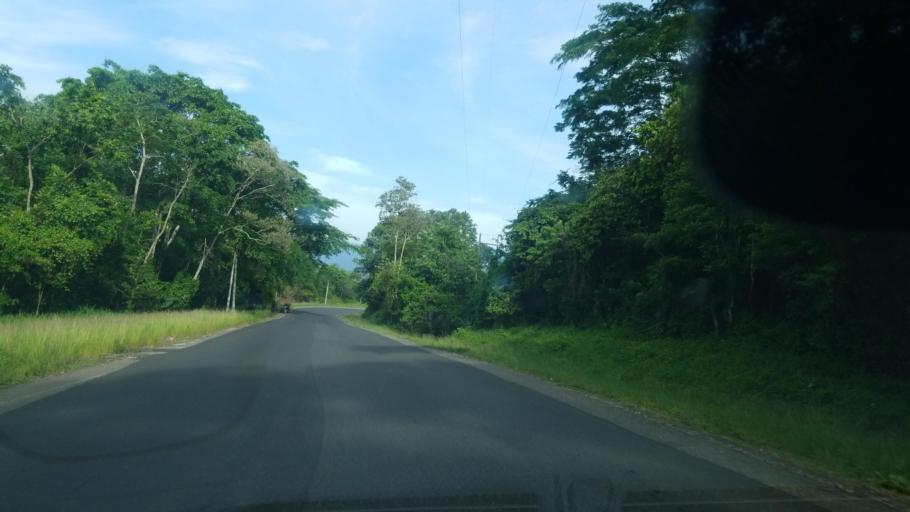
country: HN
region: Santa Barbara
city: Trinidad
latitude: 15.1749
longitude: -88.2682
